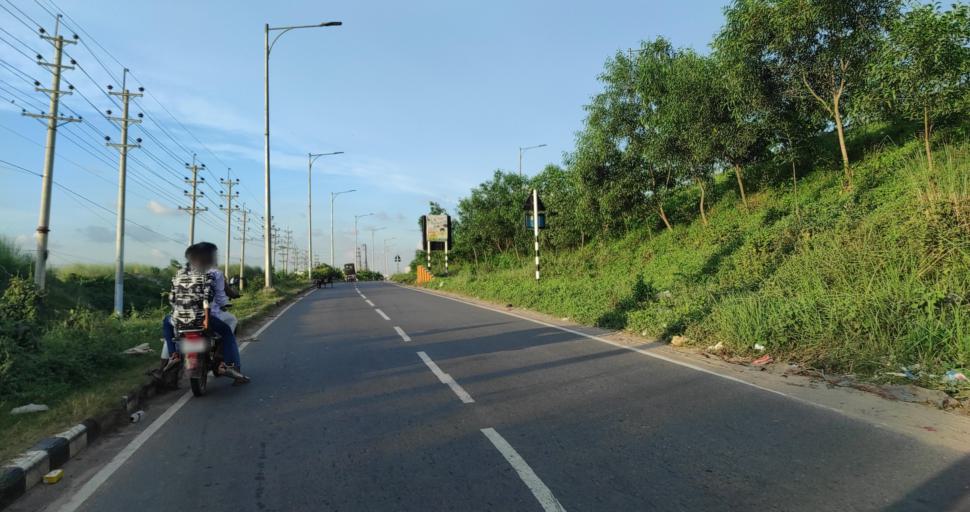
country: BD
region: Dhaka
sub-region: Dhaka
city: Dhaka
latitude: 23.6766
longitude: 90.4067
